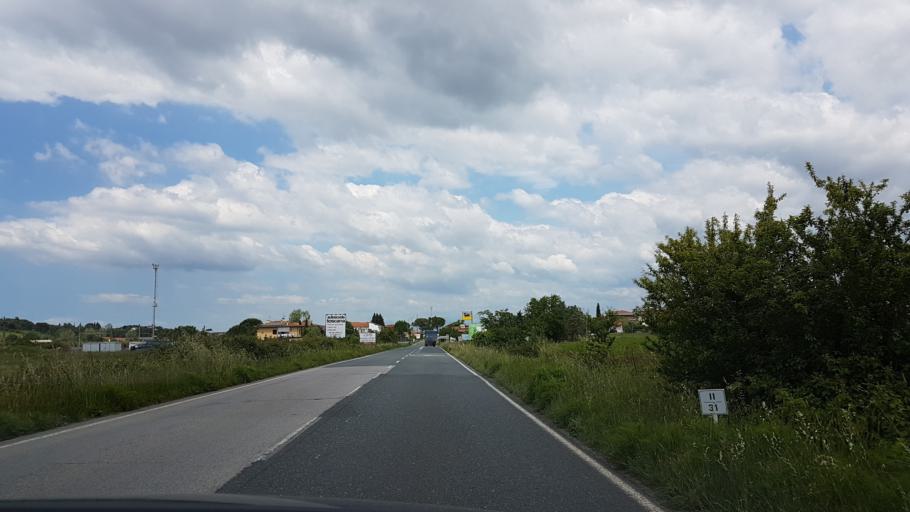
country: IT
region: Tuscany
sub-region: Provincia di Livorno
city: Collesalvetti
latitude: 43.5826
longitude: 10.4730
